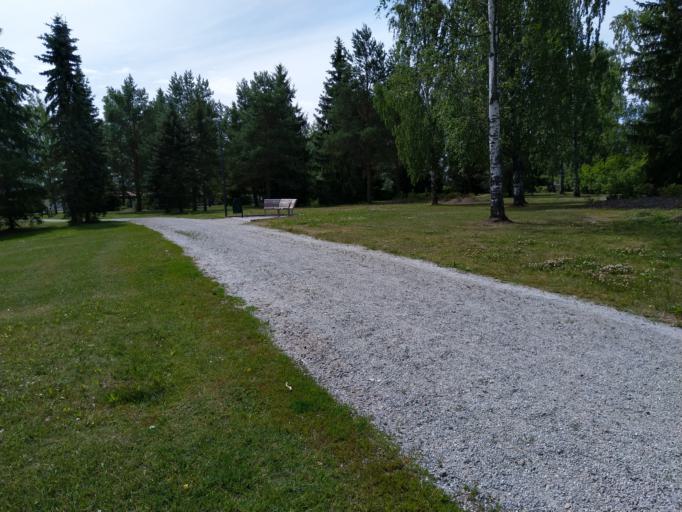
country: FI
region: Varsinais-Suomi
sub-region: Salo
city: Halikko
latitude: 60.3989
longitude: 23.0818
